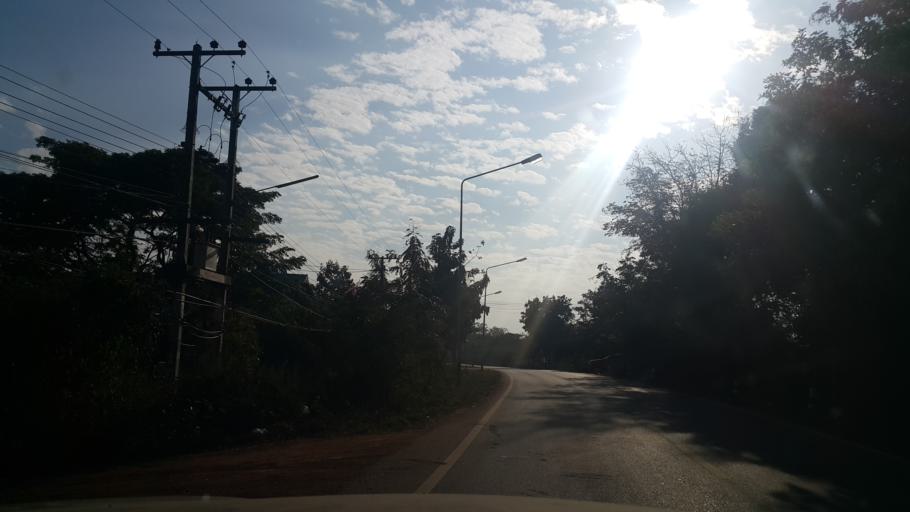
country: TH
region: Lampang
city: Ko Kha
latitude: 18.2177
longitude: 99.3418
